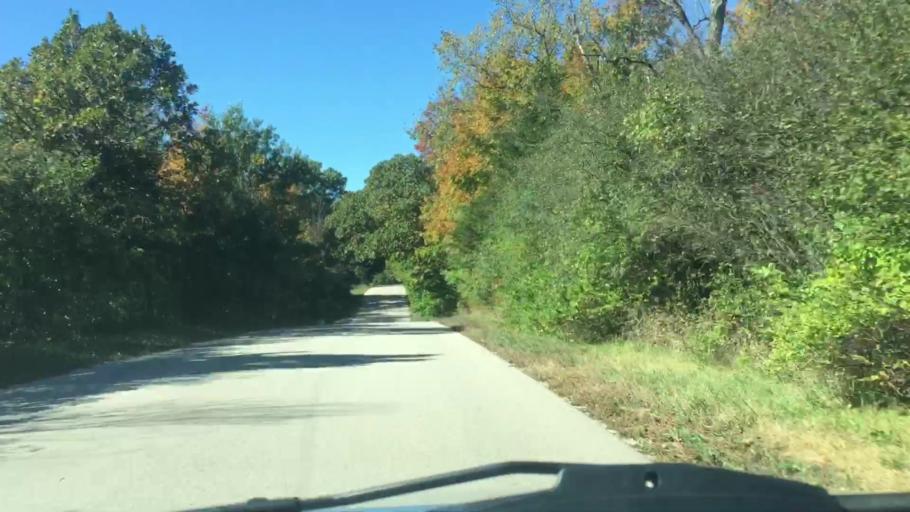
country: US
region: Wisconsin
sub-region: Waukesha County
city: North Prairie
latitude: 42.9303
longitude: -88.4478
